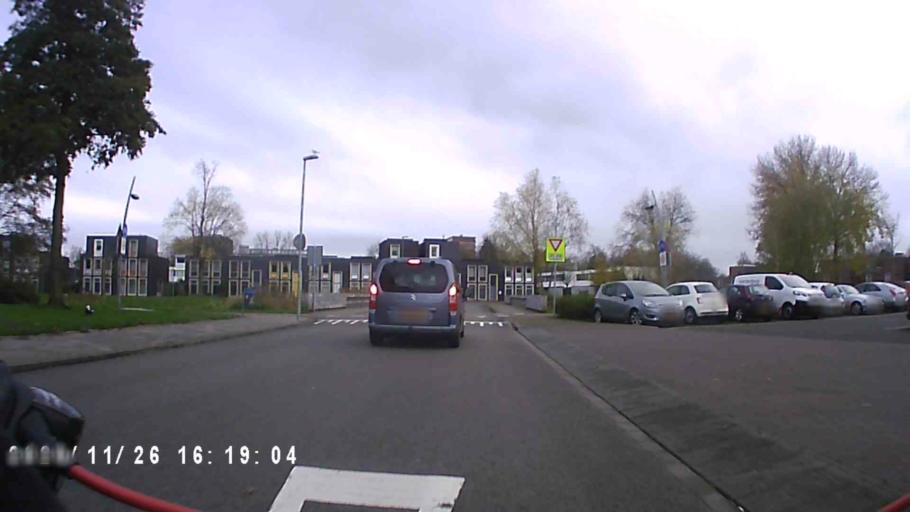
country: NL
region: Groningen
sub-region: Gemeente Groningen
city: Oosterpark
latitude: 53.2374
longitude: 6.6253
